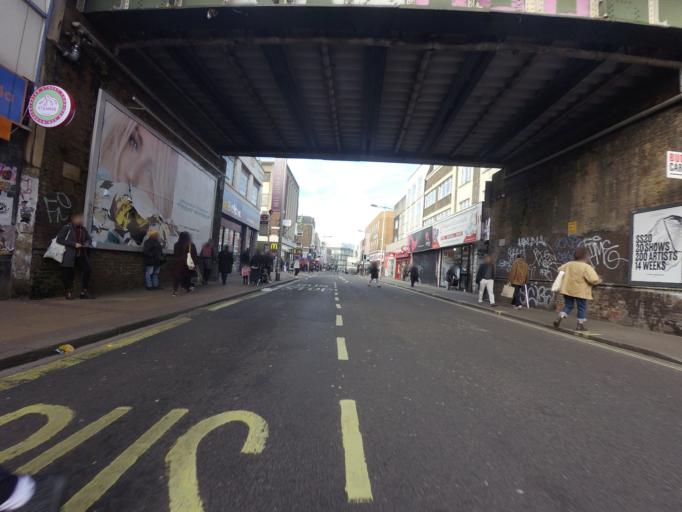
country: GB
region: England
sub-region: Greater London
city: Camberwell
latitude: 51.4704
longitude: -0.0688
